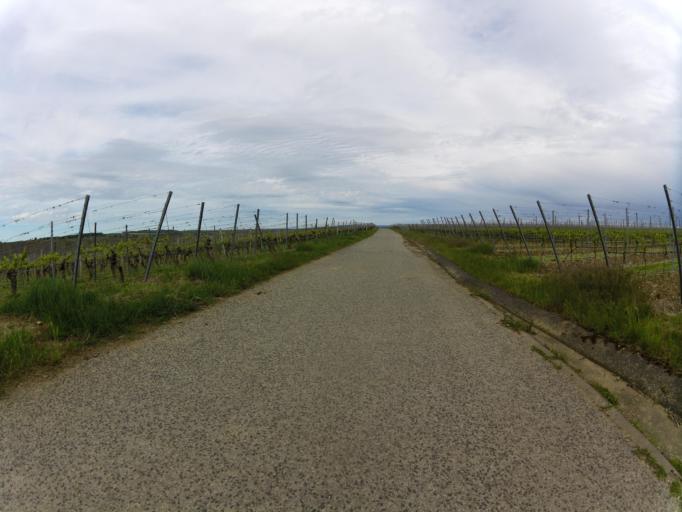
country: DE
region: Bavaria
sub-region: Regierungsbezirk Unterfranken
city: Nordheim
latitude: 49.8517
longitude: 10.1877
